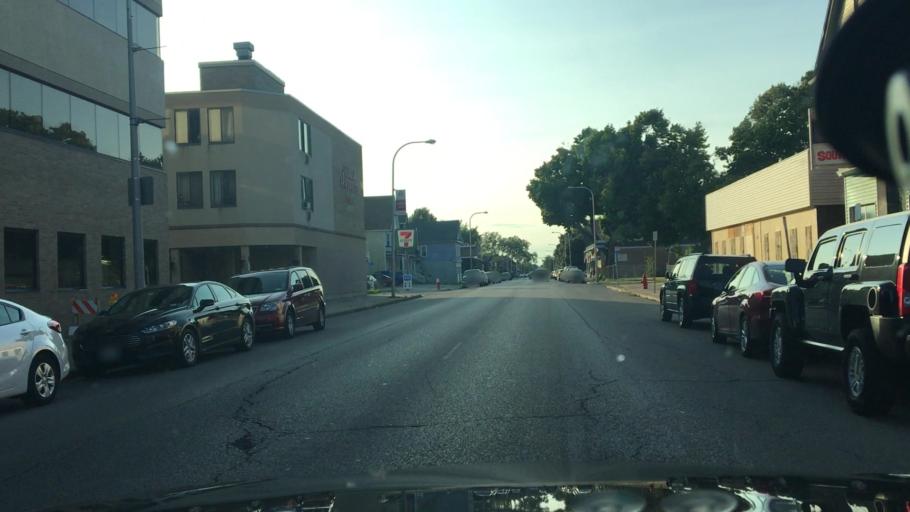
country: US
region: New York
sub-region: Erie County
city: West Seneca
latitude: 42.8492
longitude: -78.8137
